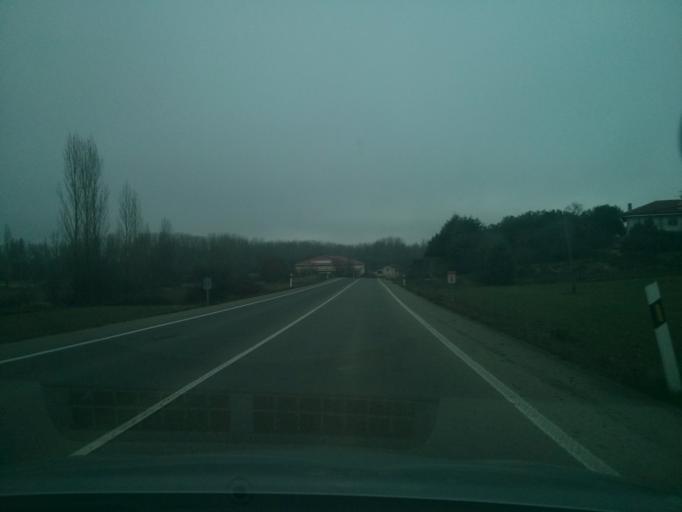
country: ES
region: Castille and Leon
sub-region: Provincia de Burgos
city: Medina de Pomar
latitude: 42.9361
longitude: -3.5220
